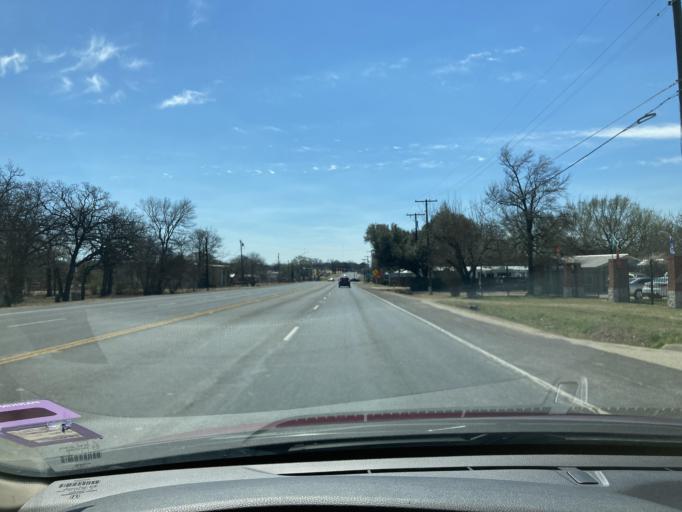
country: US
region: Texas
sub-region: Navarro County
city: Corsicana
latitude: 32.1255
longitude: -96.4661
